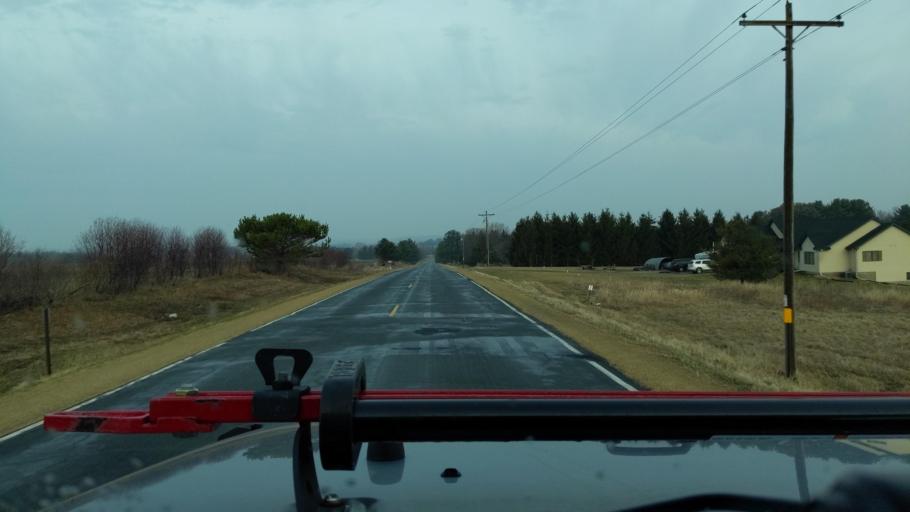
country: US
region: Wisconsin
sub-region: Saint Croix County
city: Hammond
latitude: 44.9200
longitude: -92.4461
